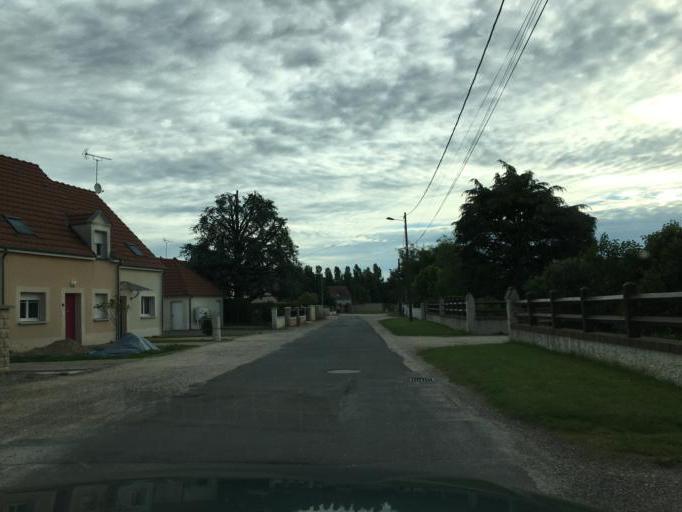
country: FR
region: Centre
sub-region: Departement du Loiret
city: Chaingy
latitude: 47.8897
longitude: 1.7754
